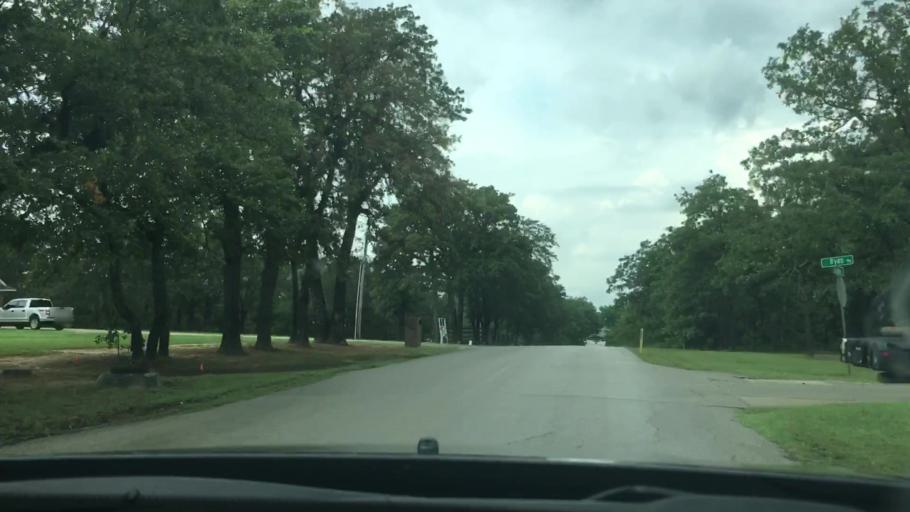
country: US
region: Oklahoma
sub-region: Carter County
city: Healdton
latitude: 34.2164
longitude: -97.4882
